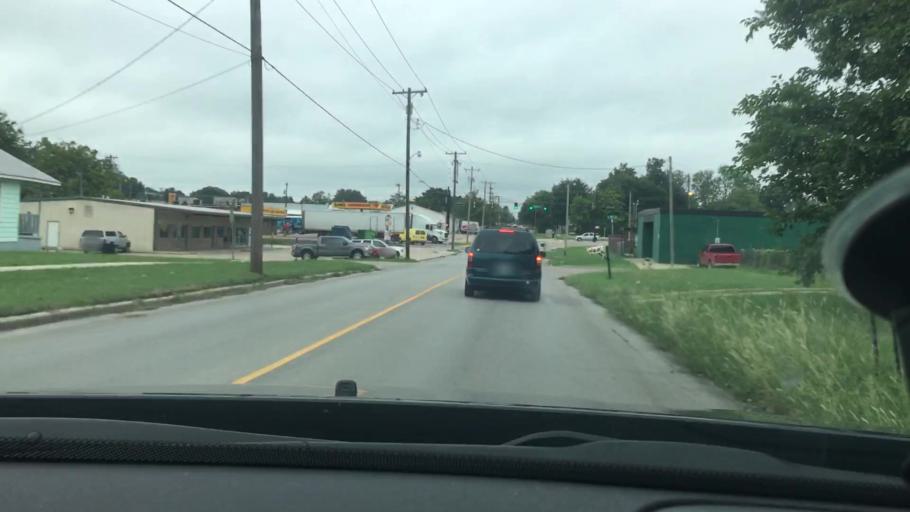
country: US
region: Oklahoma
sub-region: Pontotoc County
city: Ada
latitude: 34.7761
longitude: -96.6867
